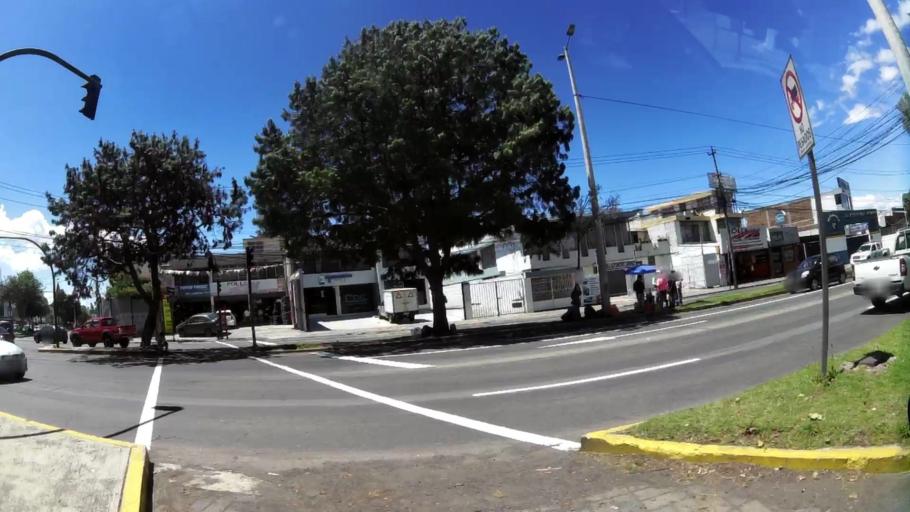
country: EC
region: Pichincha
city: Quito
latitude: -0.1605
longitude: -78.4857
